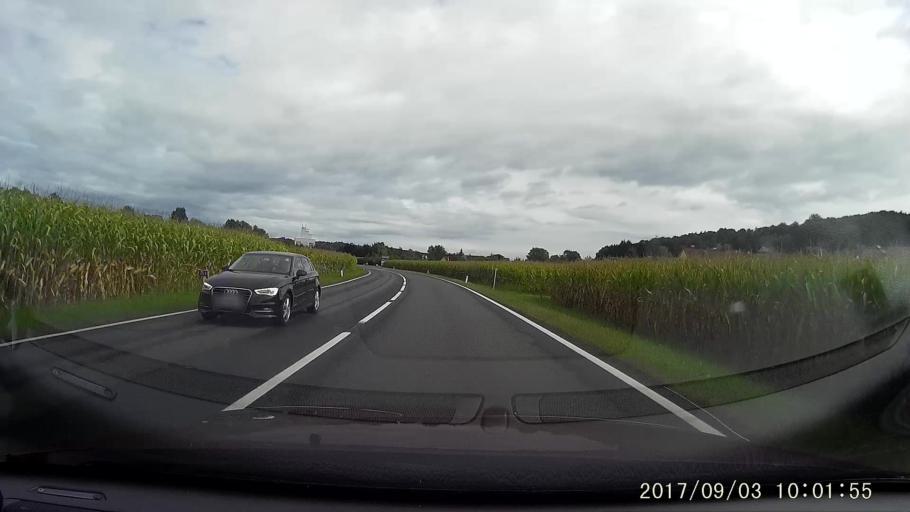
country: AT
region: Styria
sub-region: Politischer Bezirk Suedoststeiermark
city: Muehldorf bei Feldbach
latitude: 46.9393
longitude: 15.9058
